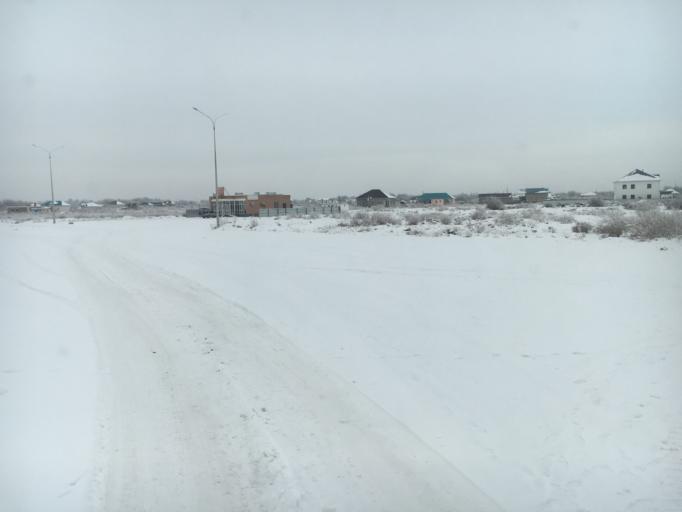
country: KZ
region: Qyzylorda
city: Tasboget
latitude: 44.7653
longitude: 65.5072
